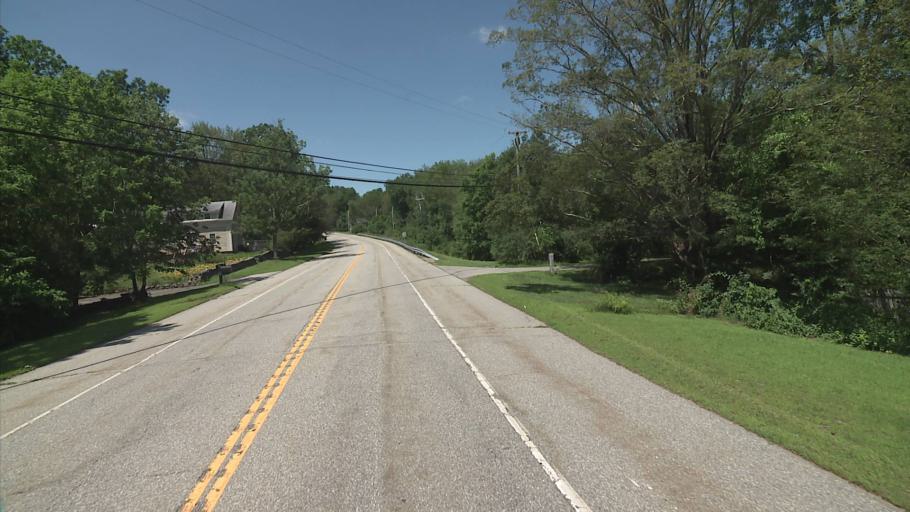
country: US
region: Connecticut
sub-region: Windham County
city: Plainfield Village
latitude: 41.7071
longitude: -71.9441
